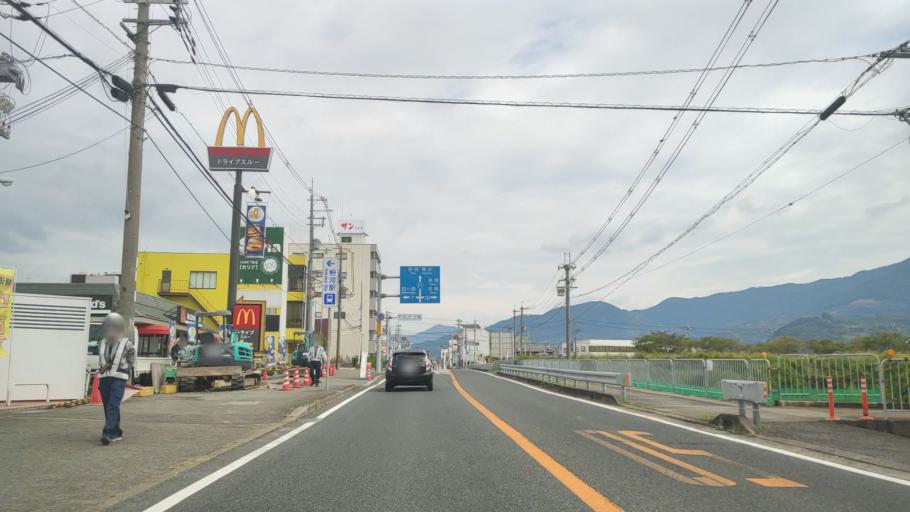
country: JP
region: Wakayama
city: Iwade
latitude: 34.2688
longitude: 135.4060
